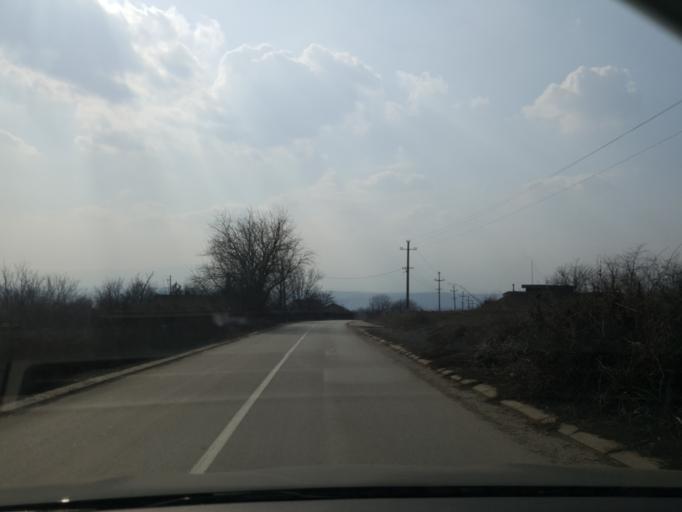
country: RS
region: Central Serbia
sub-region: Nisavski Okrug
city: Aleksinac
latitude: 43.5373
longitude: 21.7251
